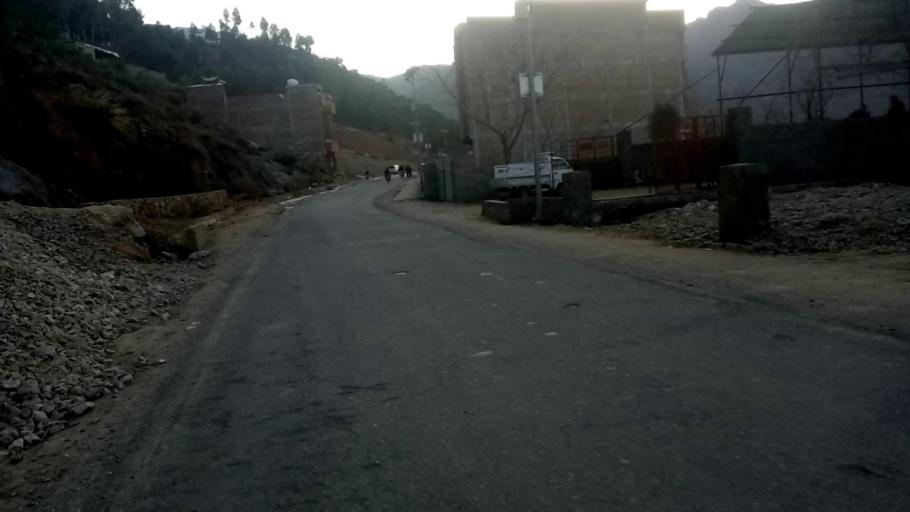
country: PK
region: Khyber Pakhtunkhwa
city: Saidu Sharif
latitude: 34.7376
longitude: 72.3394
